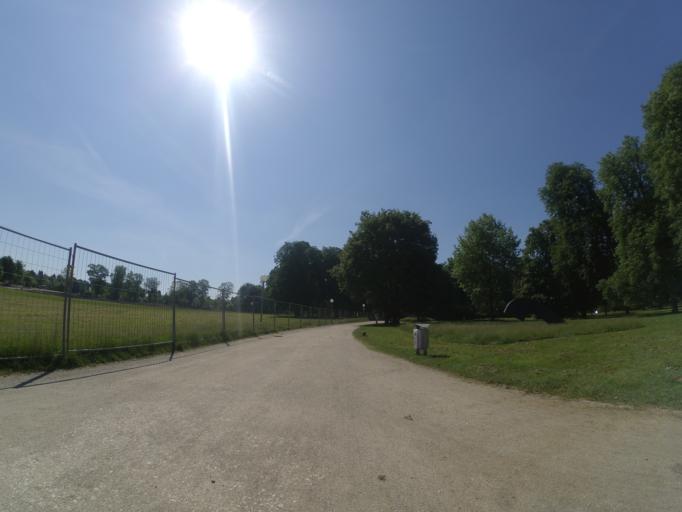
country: DE
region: Bavaria
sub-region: Swabia
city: Neu-Ulm
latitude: 48.4100
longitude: 10.0140
